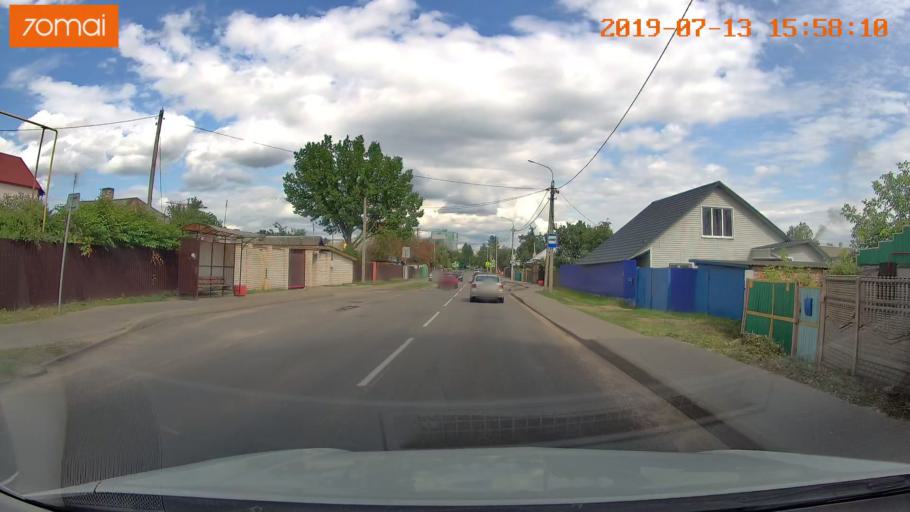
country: BY
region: Mogilev
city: Babruysk
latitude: 53.1461
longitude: 29.2087
